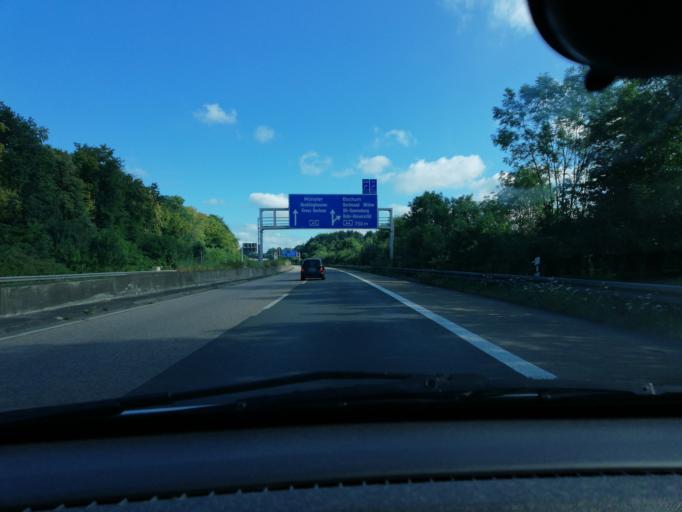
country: DE
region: North Rhine-Westphalia
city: Witten
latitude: 51.4431
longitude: 7.2941
